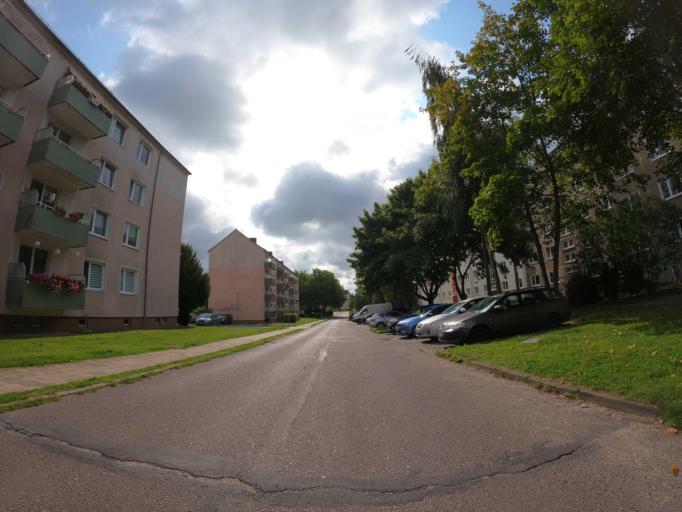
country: DE
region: Mecklenburg-Vorpommern
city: Stralsund
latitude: 54.3283
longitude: 13.0679
